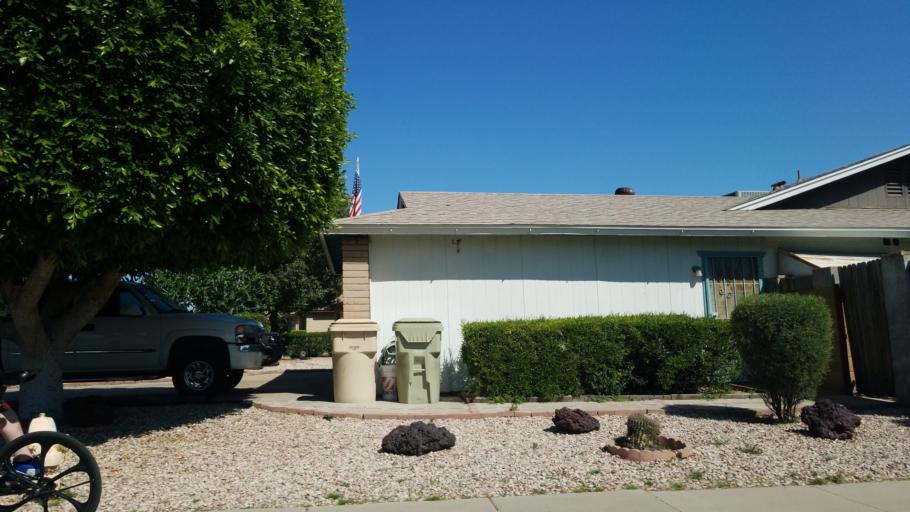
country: US
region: Arizona
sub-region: Maricopa County
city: Glendale
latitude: 33.5575
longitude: -112.1732
